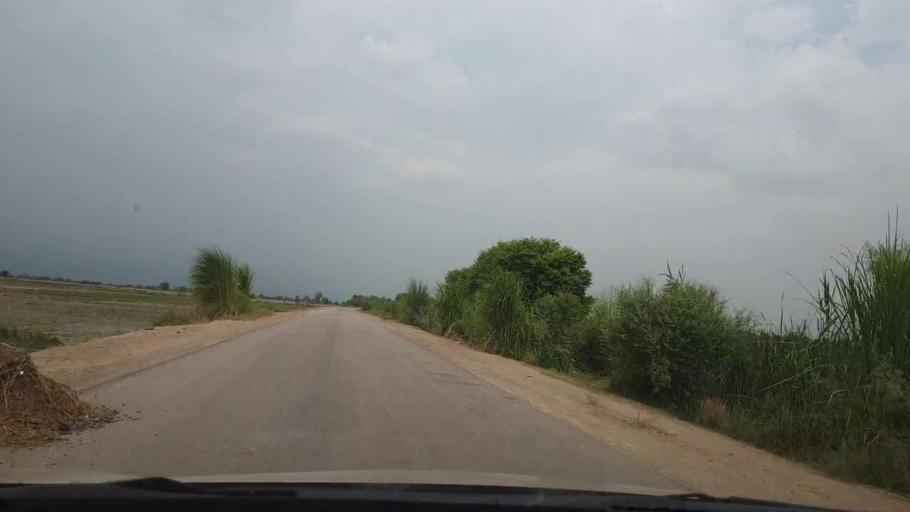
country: PK
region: Sindh
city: Ratodero
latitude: 27.8065
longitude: 68.3100
